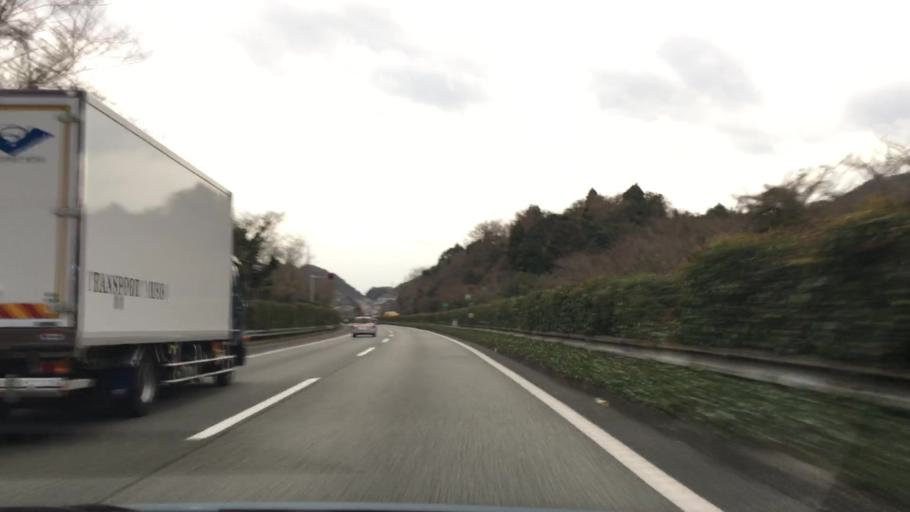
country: JP
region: Shizuoka
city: Fujinomiya
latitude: 35.1450
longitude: 138.6139
